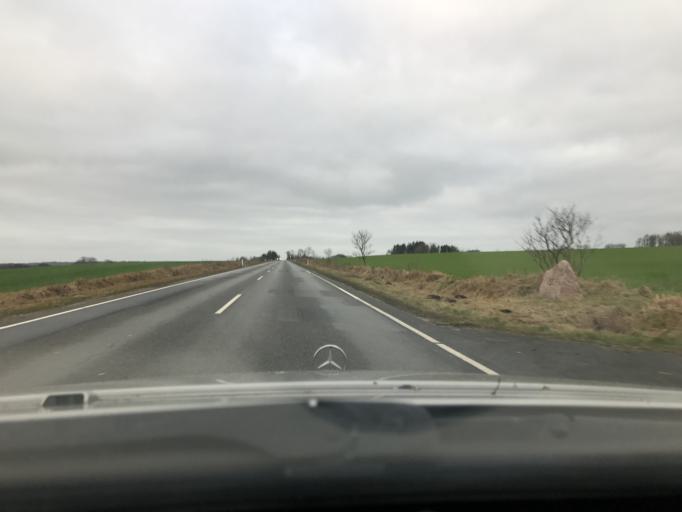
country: DK
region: South Denmark
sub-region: Tonder Kommune
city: Toftlund
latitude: 55.1786
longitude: 9.0522
